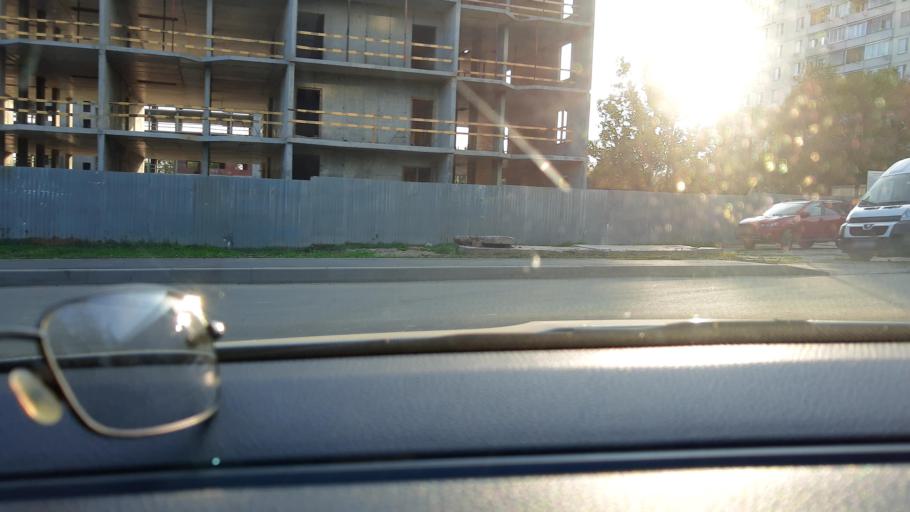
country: RU
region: Moscow
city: Vnukovo
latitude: 55.5960
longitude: 37.2010
